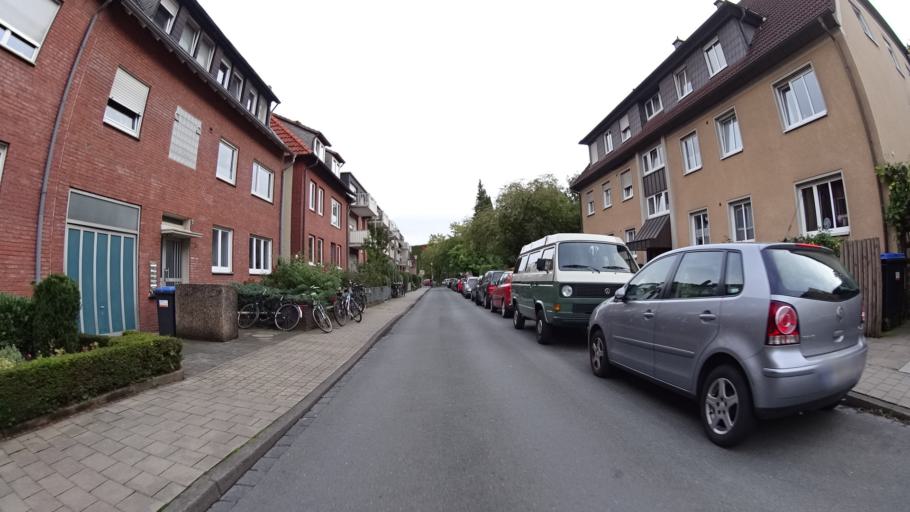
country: DE
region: North Rhine-Westphalia
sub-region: Regierungsbezirk Munster
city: Muenster
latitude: 51.9540
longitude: 7.6475
